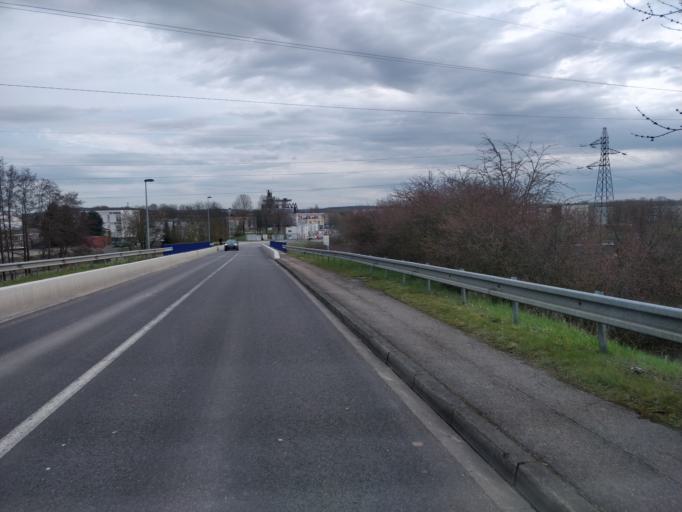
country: FR
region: Lorraine
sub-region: Departement de la Moselle
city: Uckange
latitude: 49.2984
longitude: 6.1441
